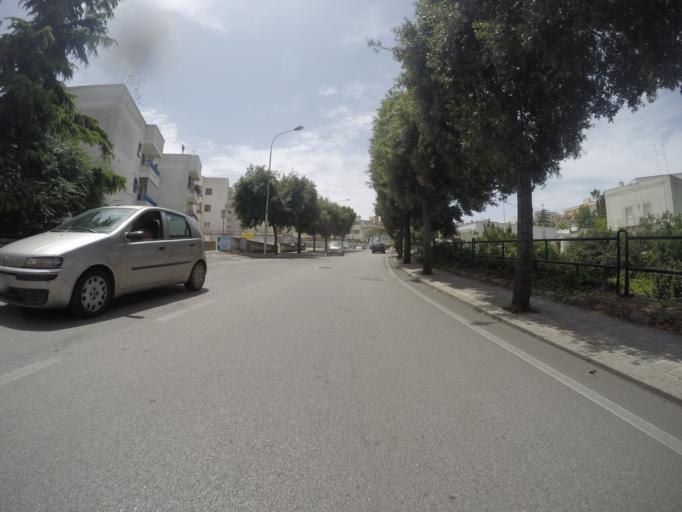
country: IT
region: Apulia
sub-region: Provincia di Taranto
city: Martina Franca
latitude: 40.7014
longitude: 17.3480
